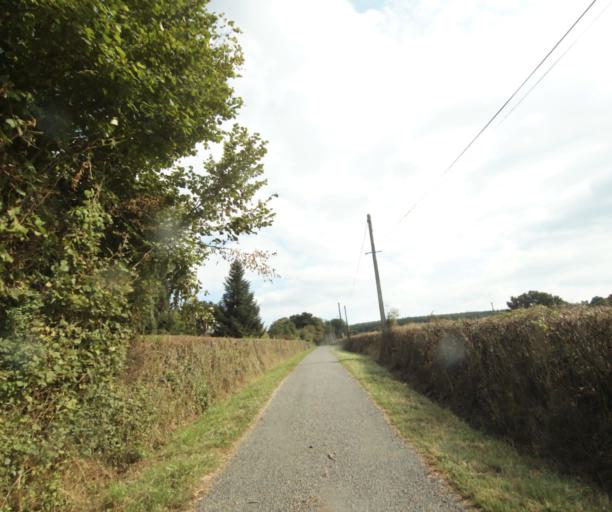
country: FR
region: Bourgogne
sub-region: Departement de Saone-et-Loire
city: Palinges
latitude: 46.5083
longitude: 4.2666
